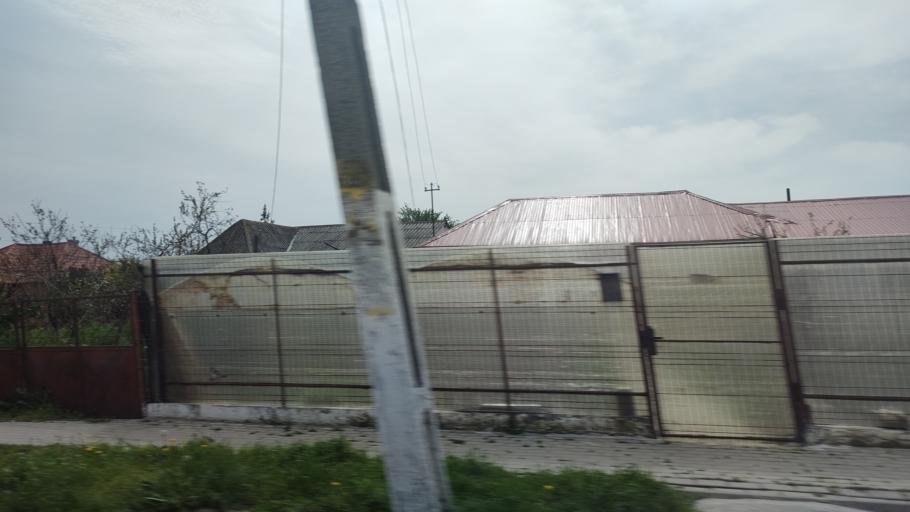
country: RO
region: Constanta
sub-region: Comuna Ciocarlia
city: Ciocarlia
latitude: 44.1055
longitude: 28.2957
